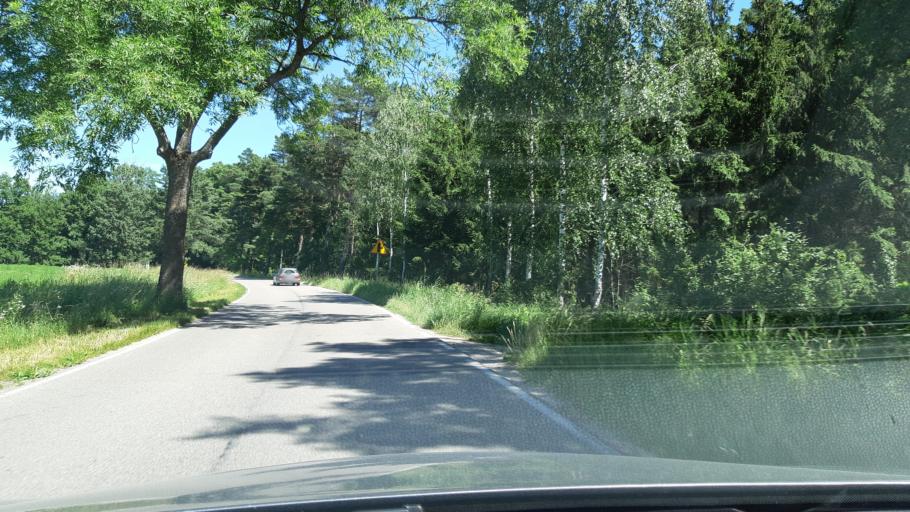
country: PL
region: Warmian-Masurian Voivodeship
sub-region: Powiat gizycki
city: Gizycko
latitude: 53.9529
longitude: 21.7304
